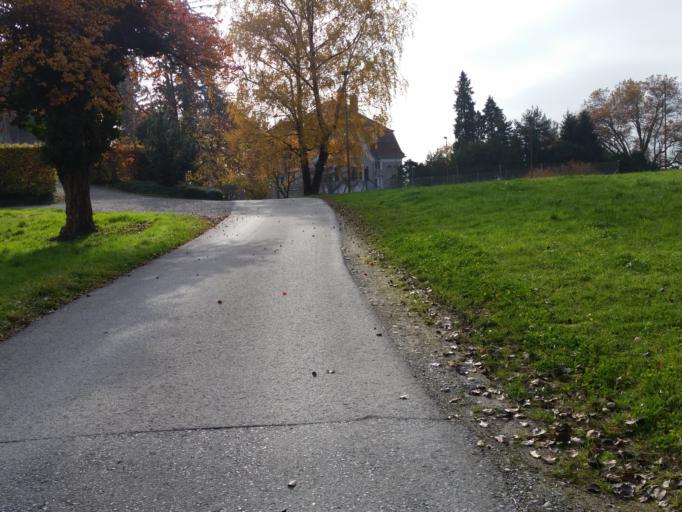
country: CH
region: Appenzell Innerrhoden
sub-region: Appenzell Inner Rhodes
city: Balgach
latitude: 47.4112
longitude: 9.6228
